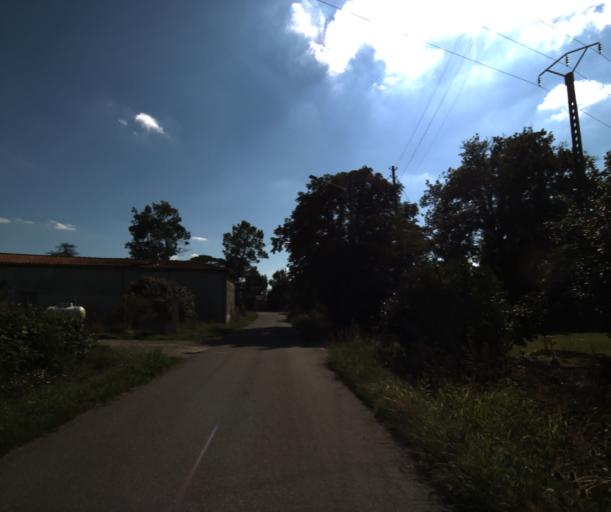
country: FR
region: Midi-Pyrenees
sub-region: Departement de la Haute-Garonne
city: Fonsorbes
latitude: 43.5087
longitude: 1.2093
